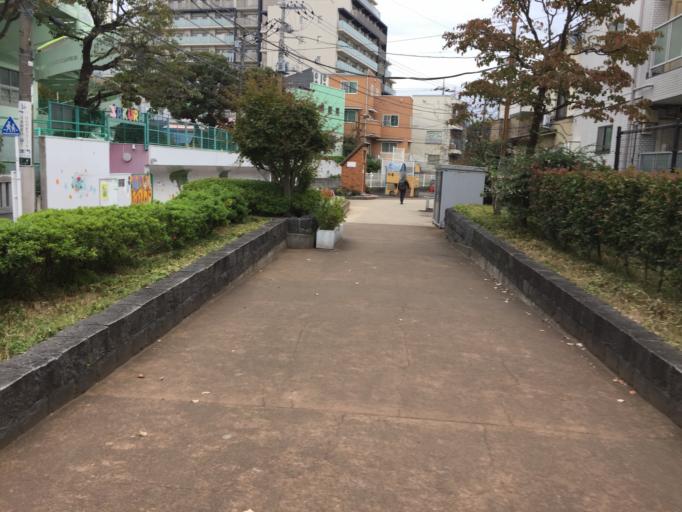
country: JP
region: Tokyo
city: Tokyo
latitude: 35.6507
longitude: 139.6743
